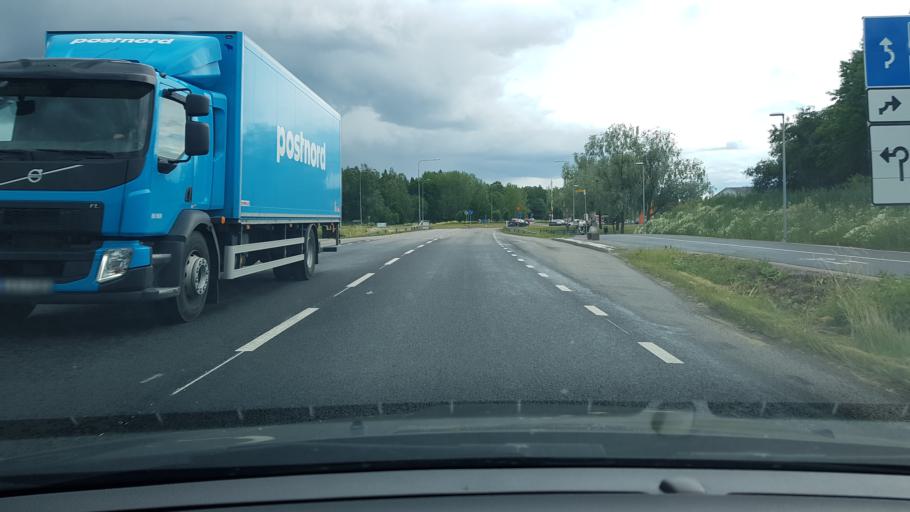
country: SE
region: Uppsala
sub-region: Uppsala Kommun
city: Saevja
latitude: 59.8222
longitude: 17.6991
